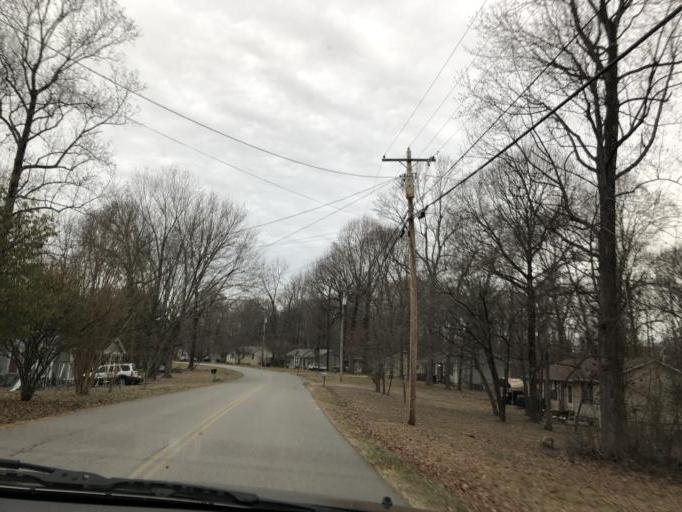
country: US
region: Tennessee
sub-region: Sumner County
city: White House
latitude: 36.4258
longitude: -86.6777
